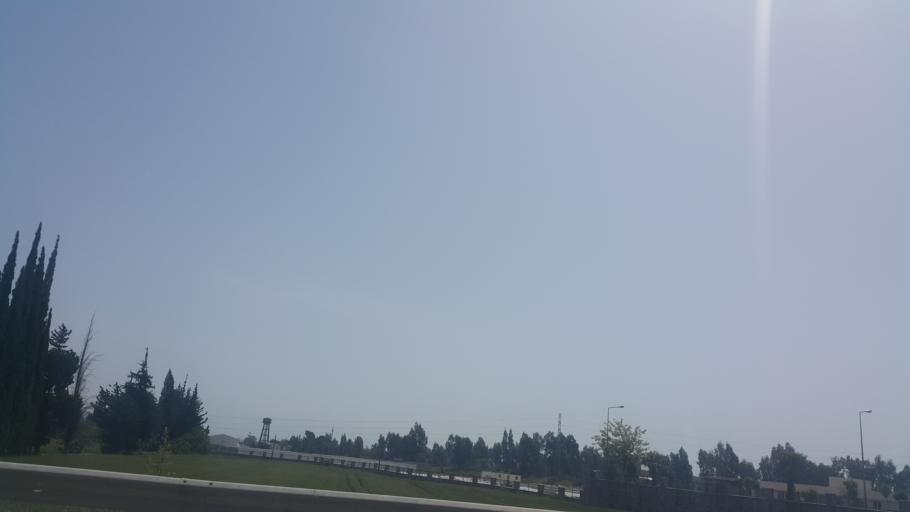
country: TR
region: Hatay
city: Serinyol
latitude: 36.3693
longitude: 36.2249
